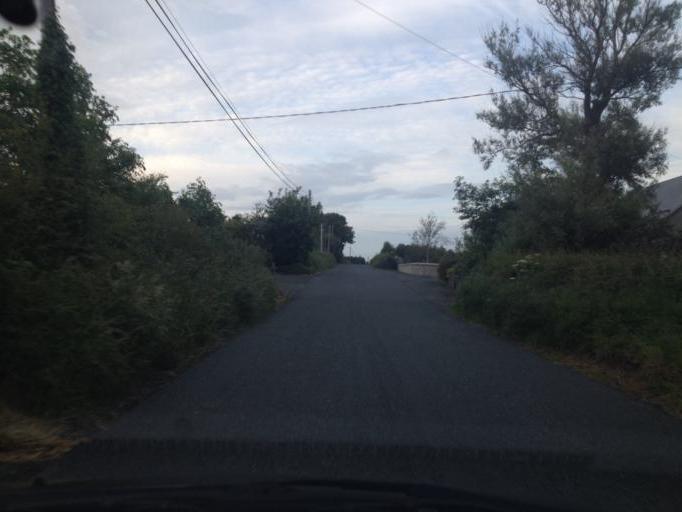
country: IE
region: Connaught
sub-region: Sligo
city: Strandhill
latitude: 54.3888
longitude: -8.5475
